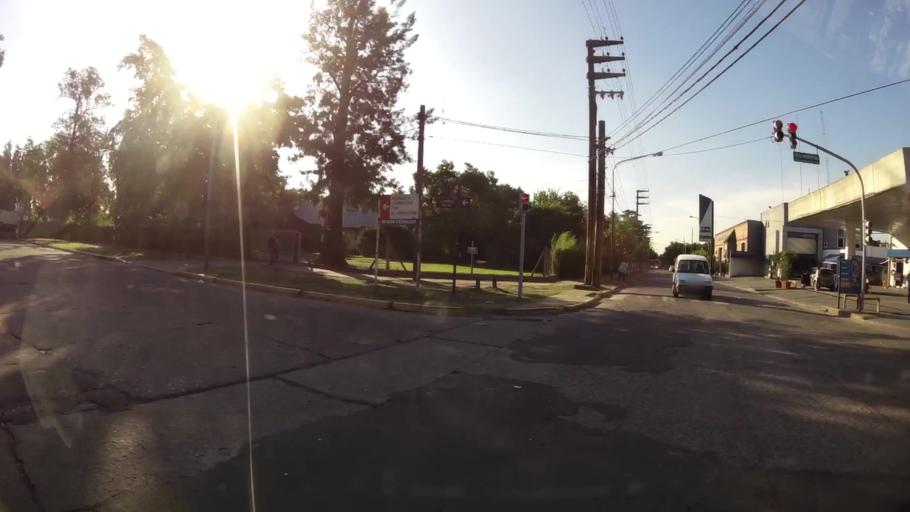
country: AR
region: Buenos Aires
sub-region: Partido de Merlo
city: Merlo
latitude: -34.6786
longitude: -58.7271
